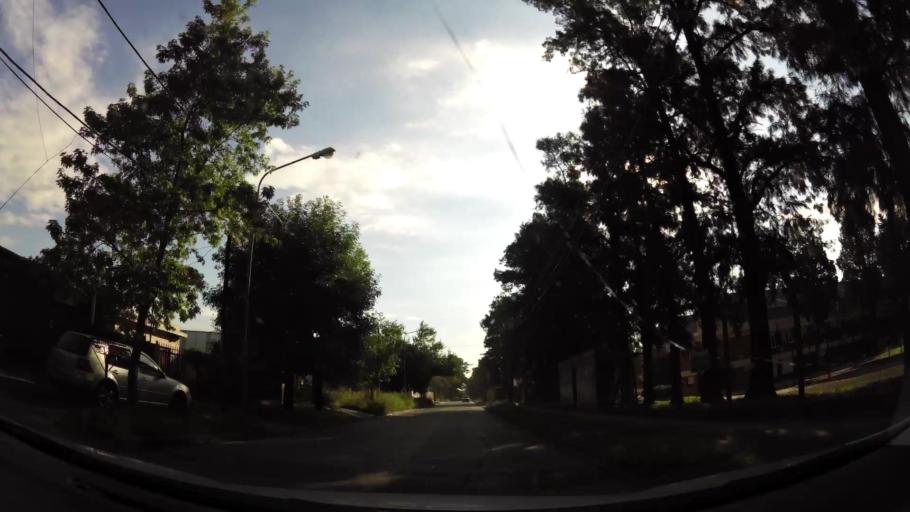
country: AR
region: Buenos Aires
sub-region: Partido de Tigre
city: Tigre
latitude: -34.4719
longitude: -58.6615
